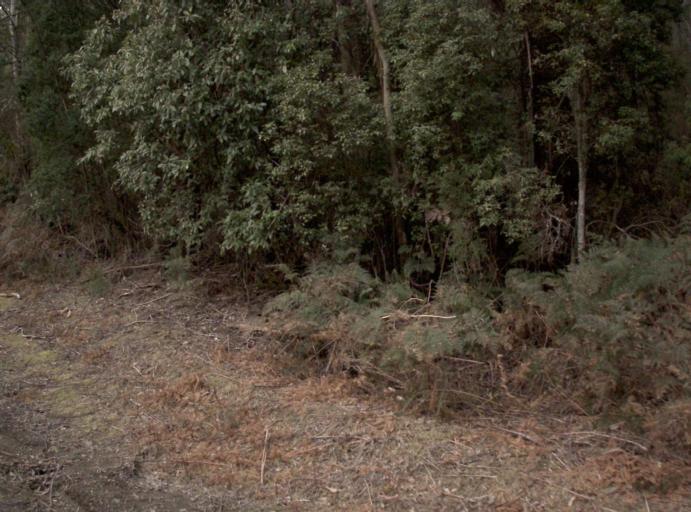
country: AU
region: Tasmania
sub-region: Dorset
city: Scottsdale
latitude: -41.2757
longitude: 147.3427
